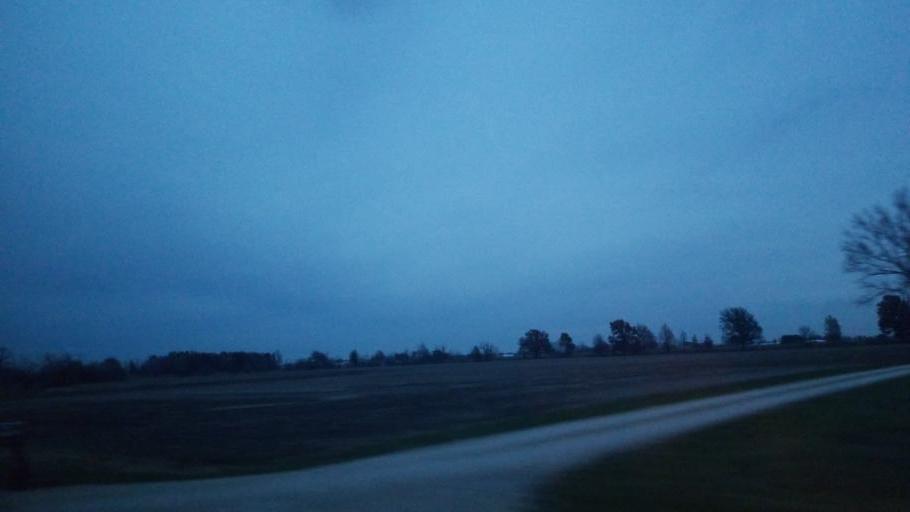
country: US
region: Indiana
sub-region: Adams County
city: Berne
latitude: 40.7154
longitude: -84.9897
